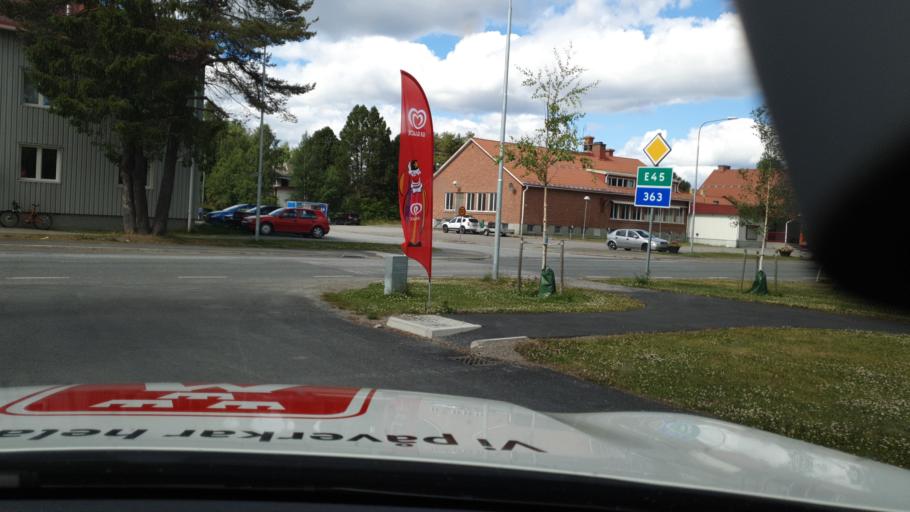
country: SE
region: Vaesterbotten
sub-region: Sorsele Kommun
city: Sorsele
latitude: 65.5354
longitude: 17.5421
